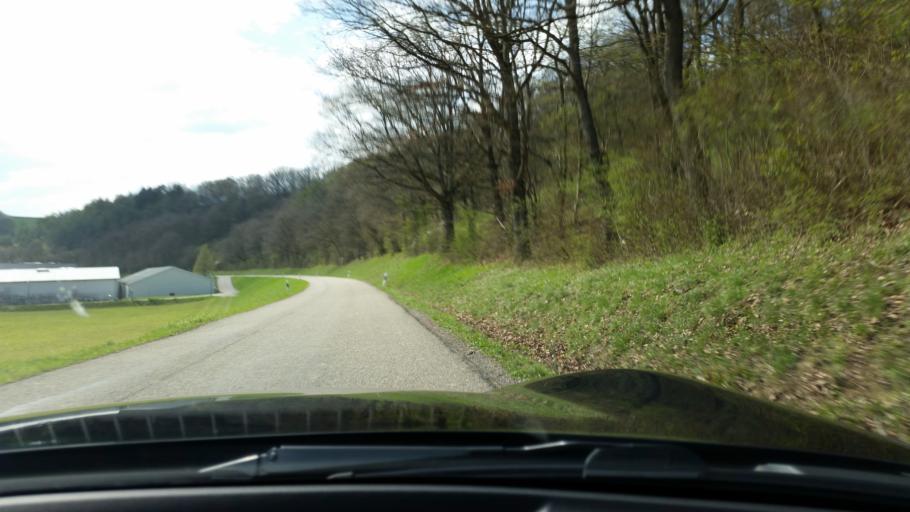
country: DE
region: Baden-Wuerttemberg
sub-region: Regierungsbezirk Stuttgart
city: Forchtenberg
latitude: 49.3538
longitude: 9.5349
